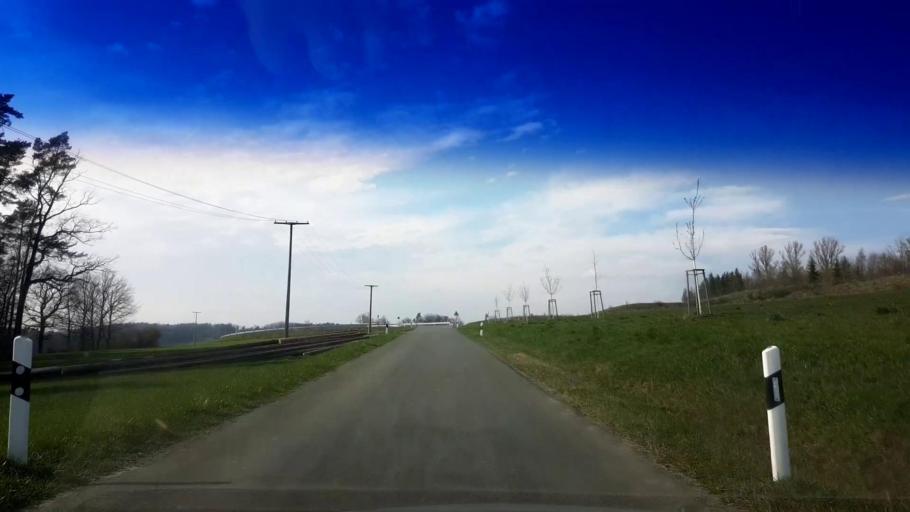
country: DE
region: Bavaria
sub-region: Upper Franconia
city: Harsdorf
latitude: 50.0262
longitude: 11.5921
